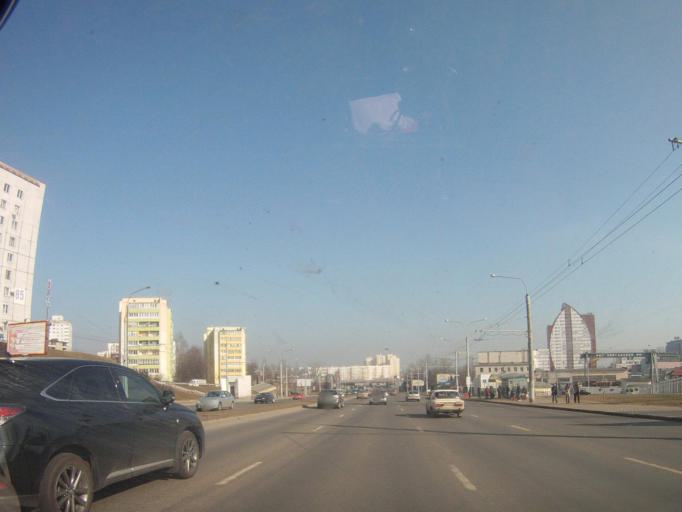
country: BY
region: Minsk
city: Novoye Medvezhino
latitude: 53.9231
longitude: 27.5020
